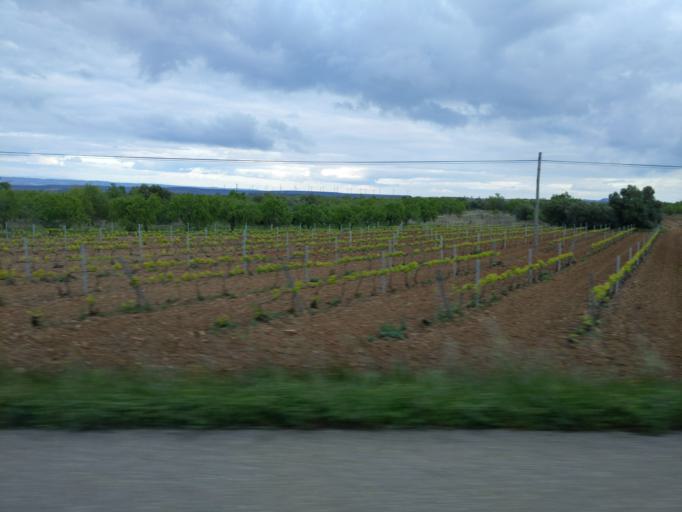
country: ES
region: La Rioja
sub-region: Provincia de La Rioja
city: Tudelilla
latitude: 42.3136
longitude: -2.0957
